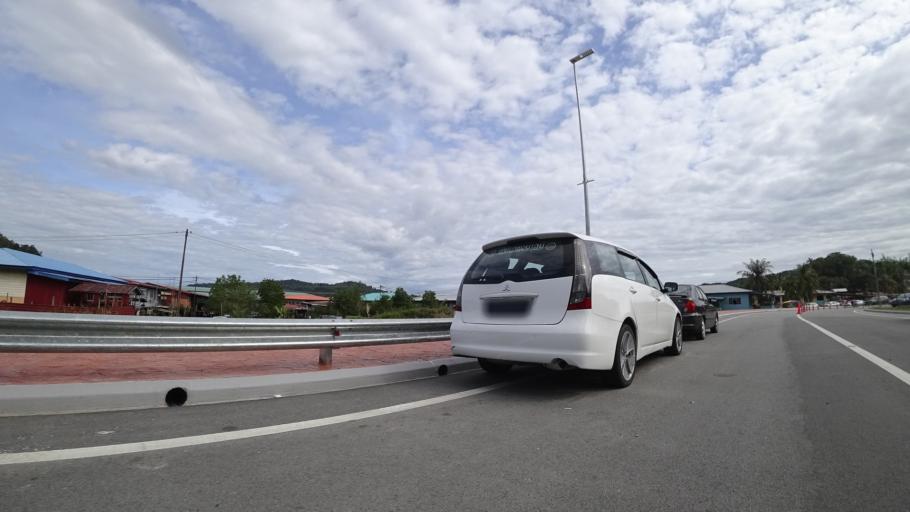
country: BN
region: Brunei and Muara
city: Bandar Seri Begawan
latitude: 4.8736
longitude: 114.9455
